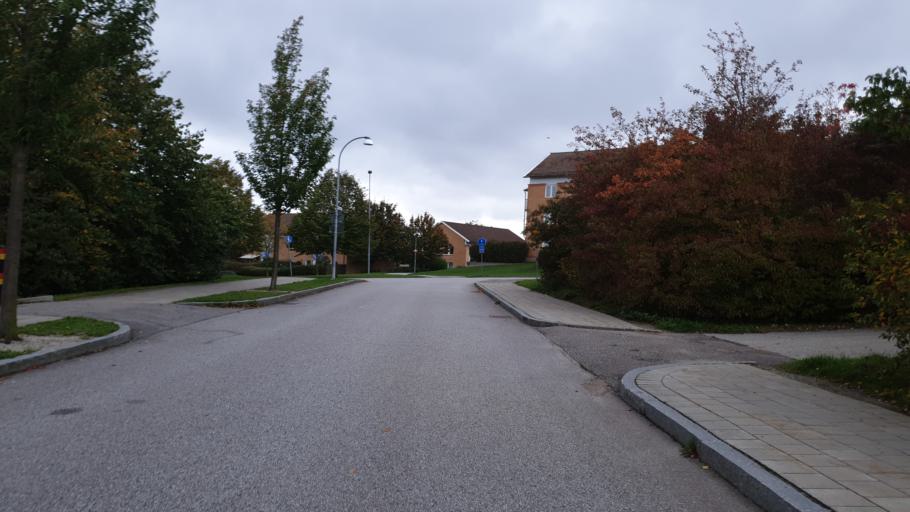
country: SE
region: Skane
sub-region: Lunds Kommun
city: Lund
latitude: 55.7126
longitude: 13.2426
